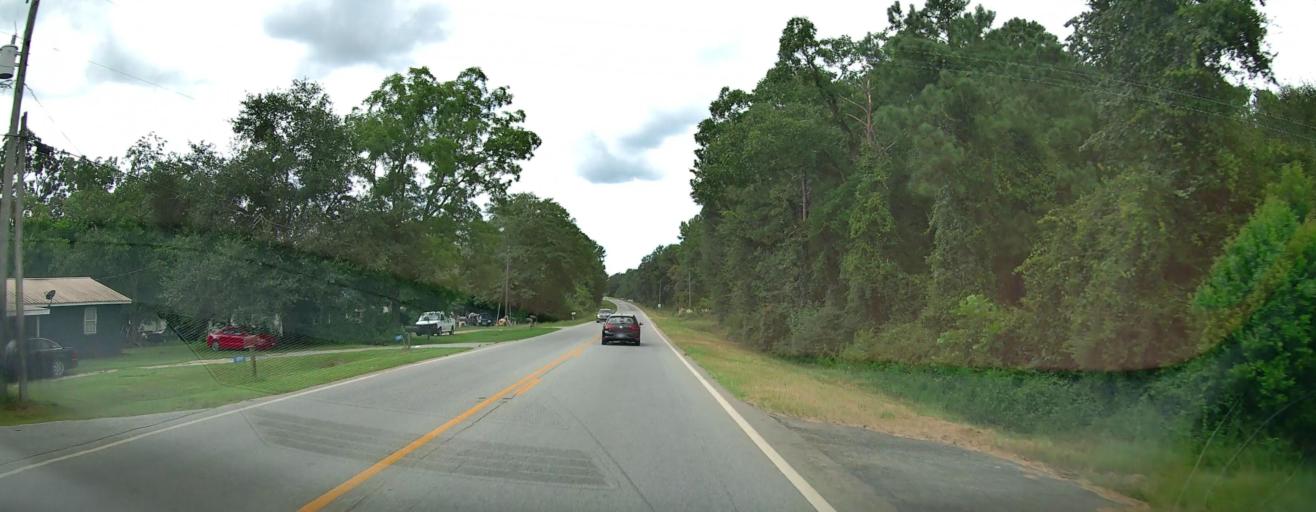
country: US
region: Georgia
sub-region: Macon County
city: Oglethorpe
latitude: 32.2729
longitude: -84.0723
